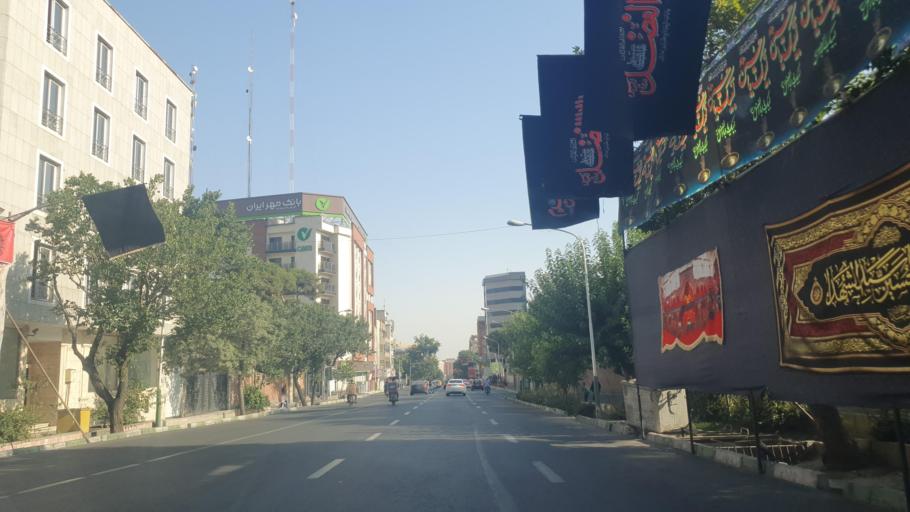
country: IR
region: Tehran
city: Tehran
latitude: 35.7088
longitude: 51.4256
